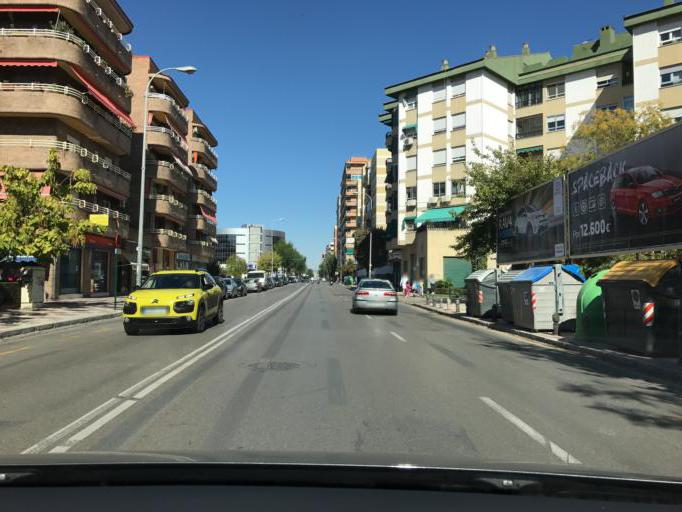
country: ES
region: Andalusia
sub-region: Provincia de Granada
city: Granada
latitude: 37.1657
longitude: -3.6046
